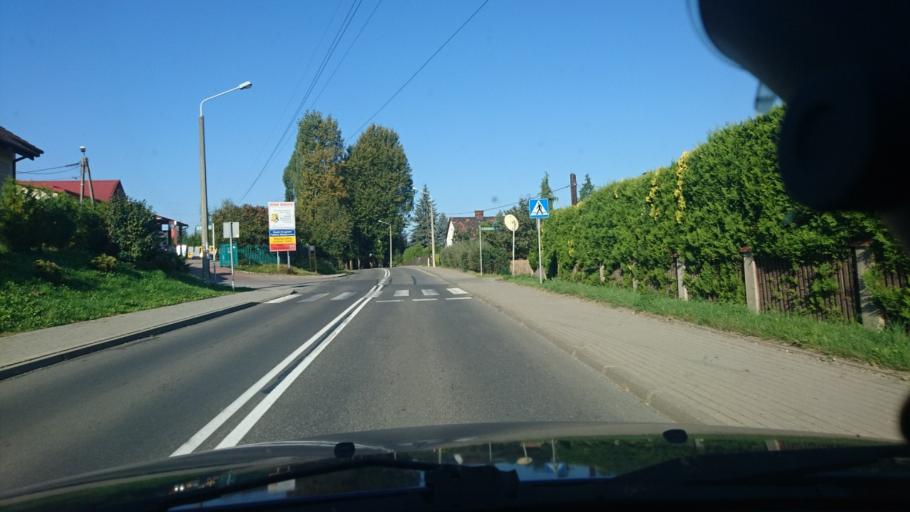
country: PL
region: Silesian Voivodeship
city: Janowice
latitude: 49.8511
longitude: 19.0790
